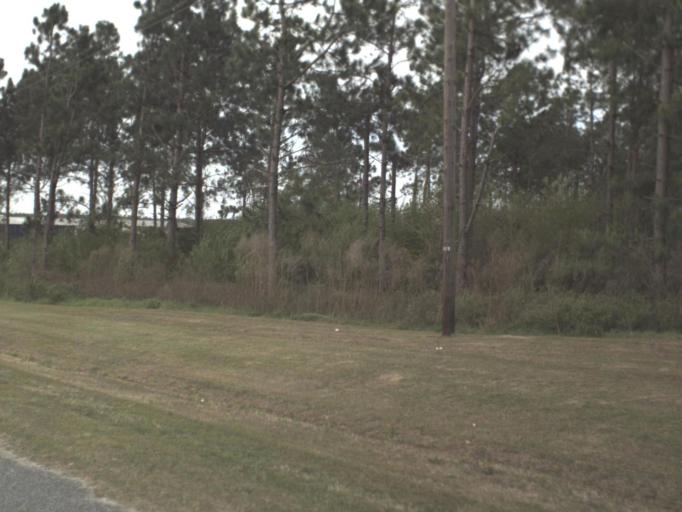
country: US
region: Florida
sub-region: Jackson County
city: Graceville
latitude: 30.9535
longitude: -85.6487
